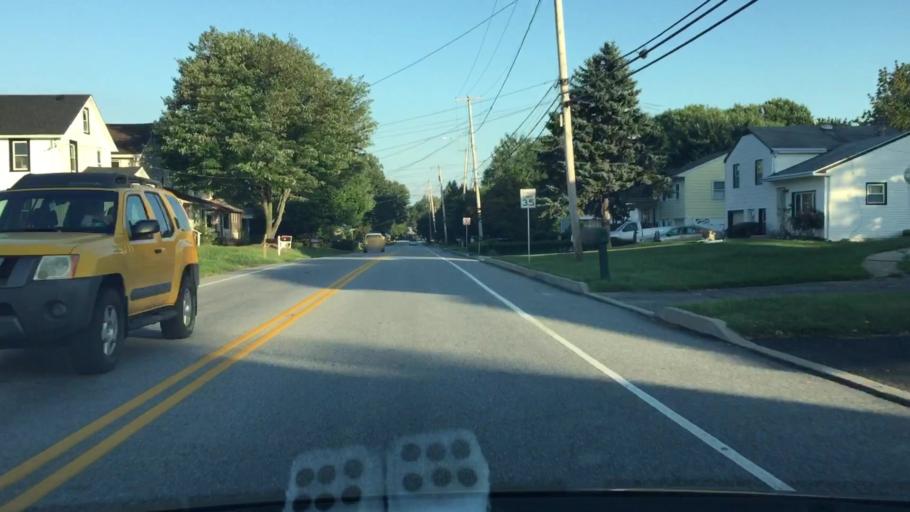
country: US
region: Pennsylvania
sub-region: Delaware County
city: Boothwyn
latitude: 39.8272
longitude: -75.4523
